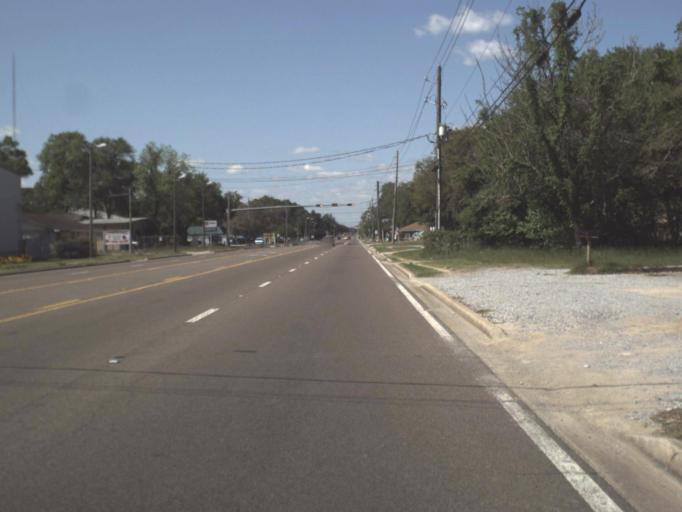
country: US
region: Florida
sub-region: Escambia County
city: Goulding
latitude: 30.4570
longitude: -87.2232
